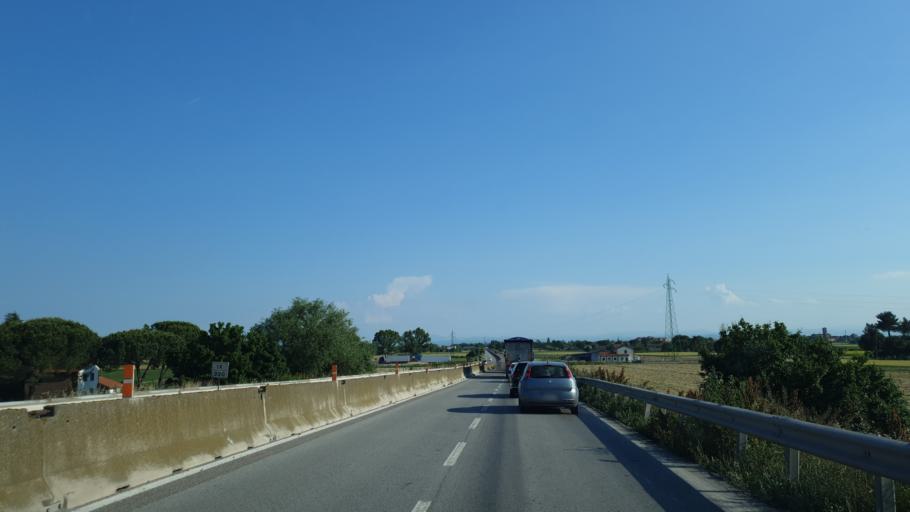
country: IT
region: Emilia-Romagna
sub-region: Provincia di Ravenna
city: Porto Fuori
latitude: 44.3974
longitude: 12.2435
